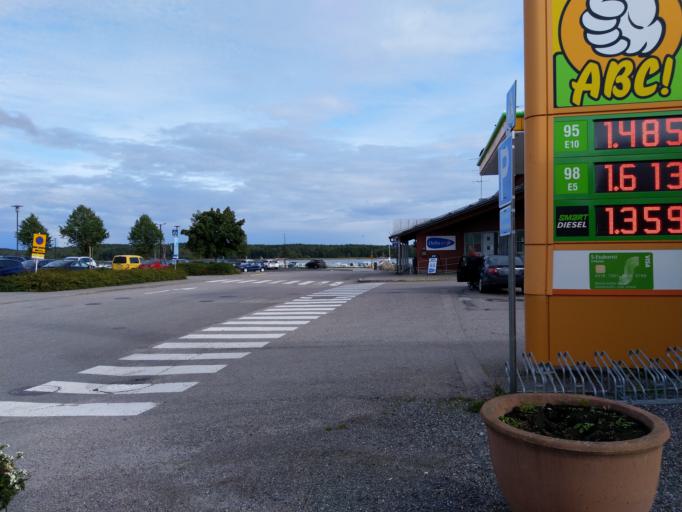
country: FI
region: Uusimaa
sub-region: Raaseporin
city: Inga
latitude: 60.0429
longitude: 24.0057
